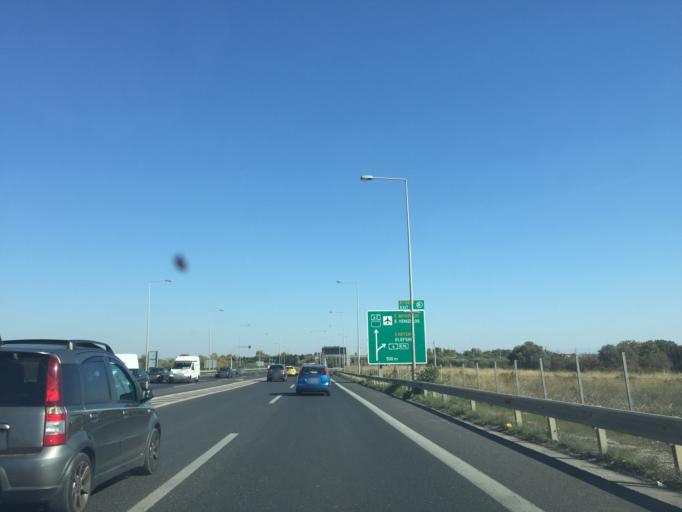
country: GR
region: Attica
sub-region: Nomarchia Anatolikis Attikis
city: Koropi
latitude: 37.9036
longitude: 23.8953
